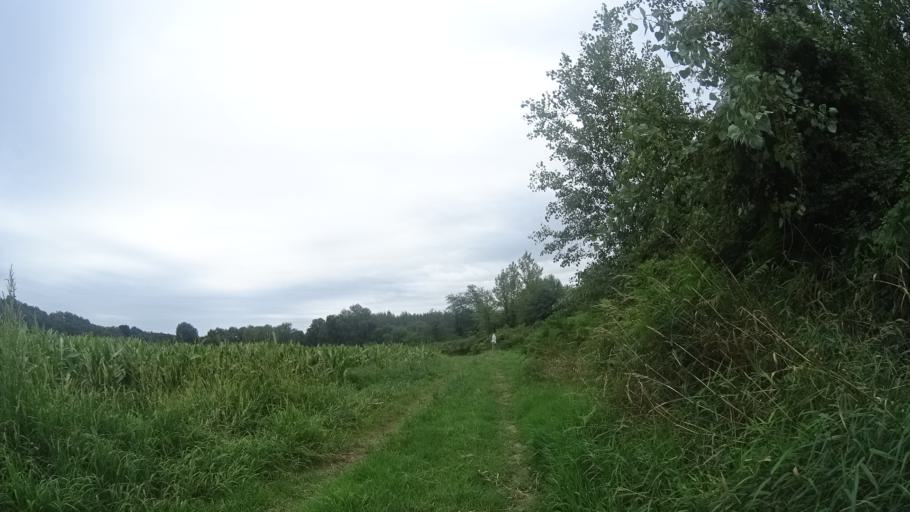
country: FR
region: Aquitaine
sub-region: Departement des Pyrenees-Atlantiques
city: Orthez
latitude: 43.4616
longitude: -0.7163
